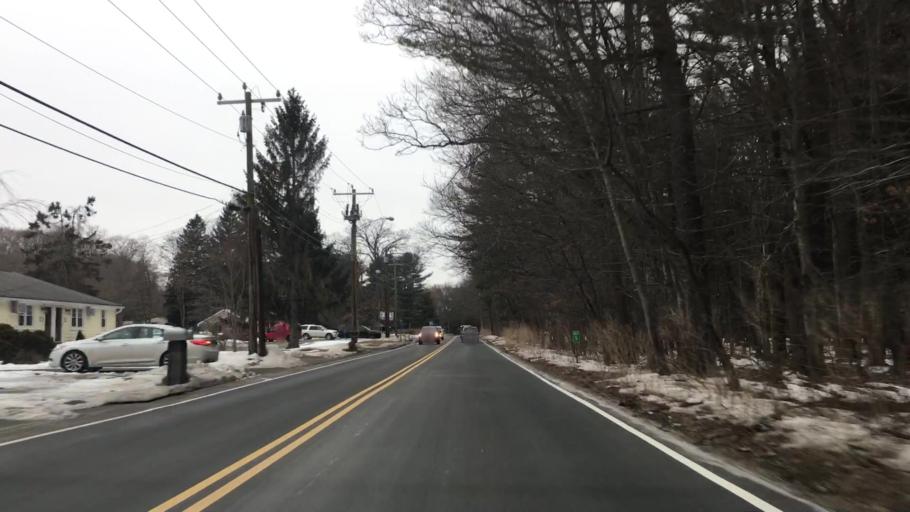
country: US
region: Massachusetts
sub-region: Hampden County
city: Westfield
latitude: 42.1023
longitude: -72.6903
